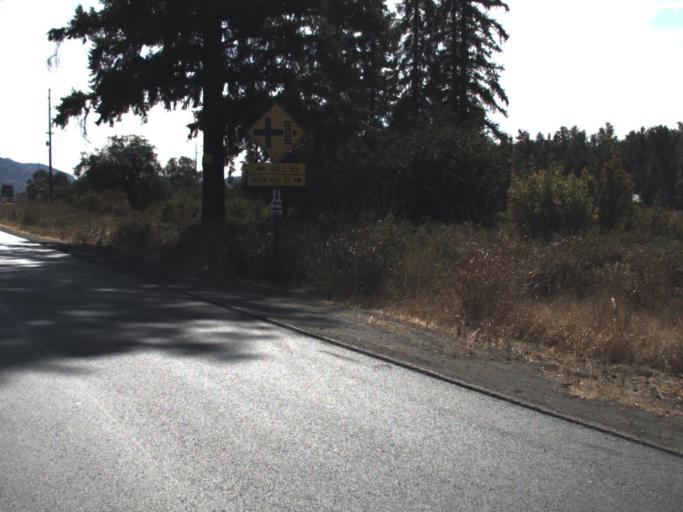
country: US
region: Washington
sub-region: Stevens County
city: Colville
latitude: 48.4615
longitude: -117.8829
